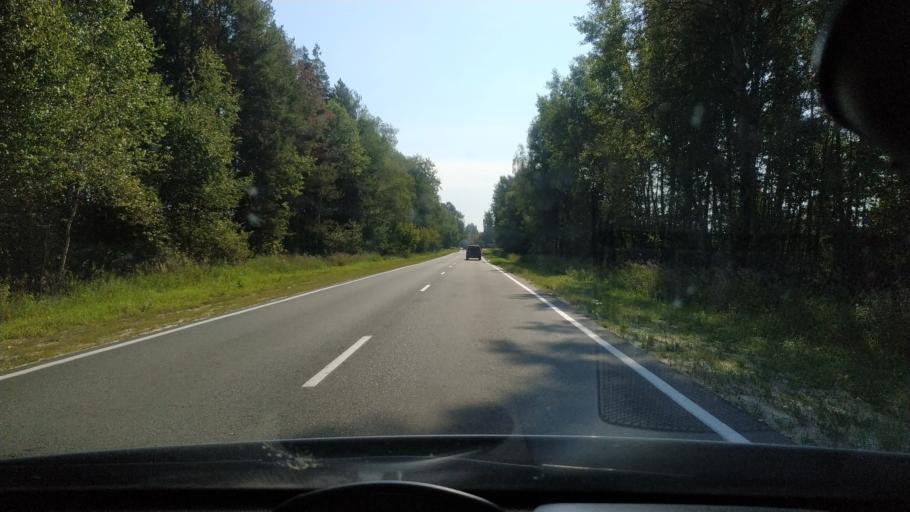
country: RU
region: Rjazan
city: Spas-Klepiki
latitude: 55.2210
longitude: 40.0855
